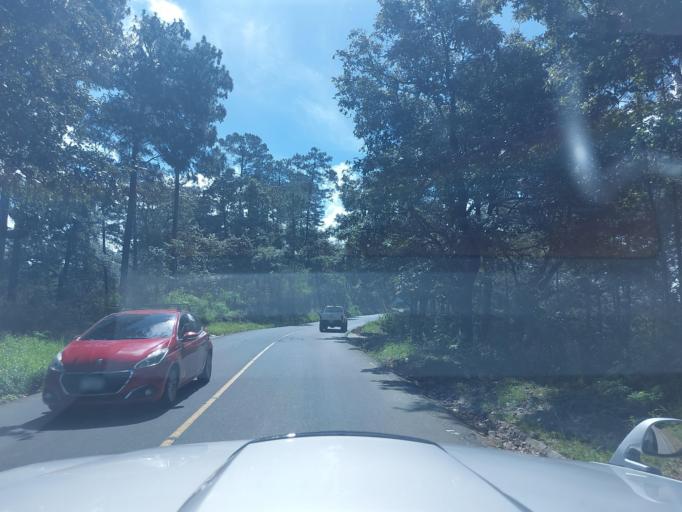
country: GT
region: Chimaltenango
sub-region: Municipio de Santa Cruz Balanya
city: Santa Cruz Balanya
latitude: 14.6995
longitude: -90.9047
